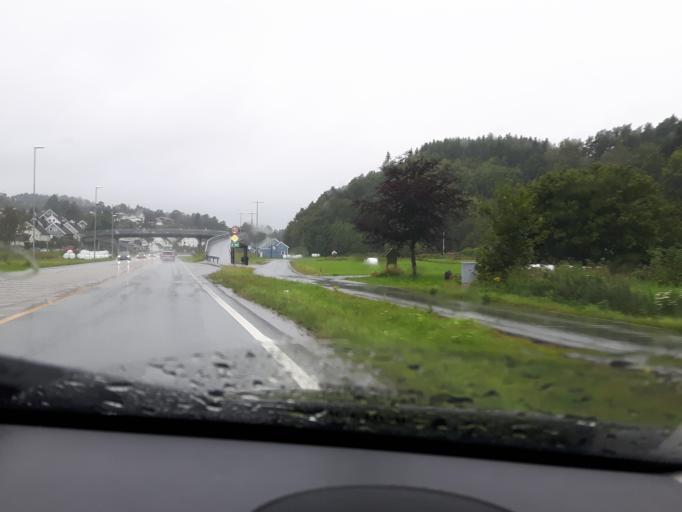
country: NO
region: Vest-Agder
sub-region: Mandal
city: Mandal
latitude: 58.0352
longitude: 7.5027
